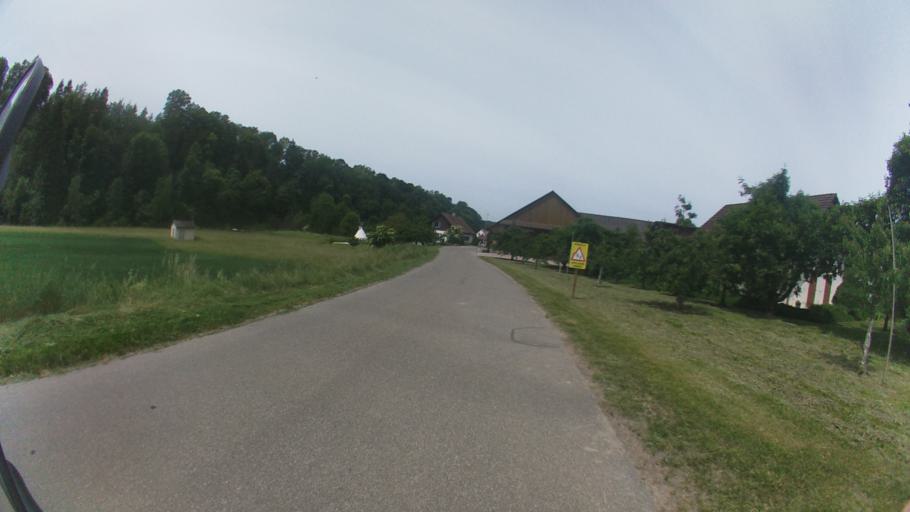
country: CH
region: Aargau
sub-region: Bezirk Zurzach
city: Tegerfelden
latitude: 47.5540
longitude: 8.2918
